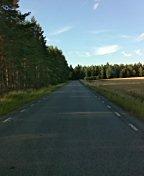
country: SE
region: Uppsala
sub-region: Habo Kommun
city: Balsta
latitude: 59.6859
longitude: 17.5345
